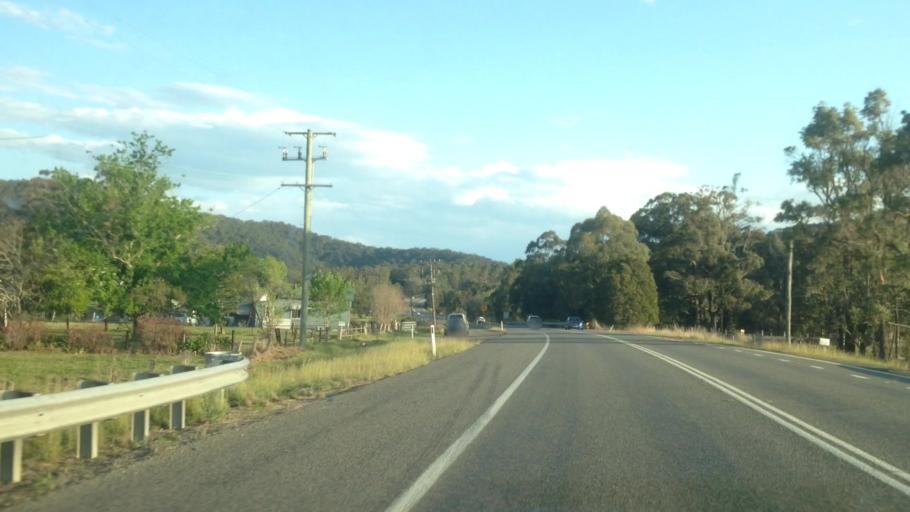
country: AU
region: New South Wales
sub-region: Lake Macquarie Shire
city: Holmesville
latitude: -32.9491
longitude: 151.4790
